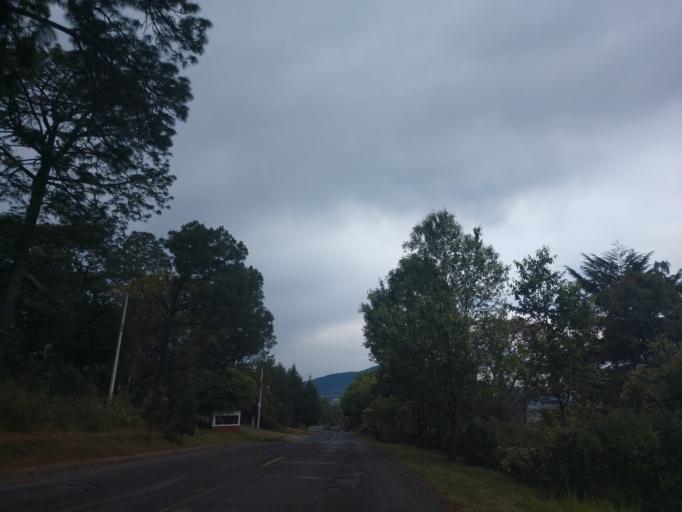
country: MX
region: Jalisco
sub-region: Mazamitla
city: Mazamitla
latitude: 19.9212
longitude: -103.0352
